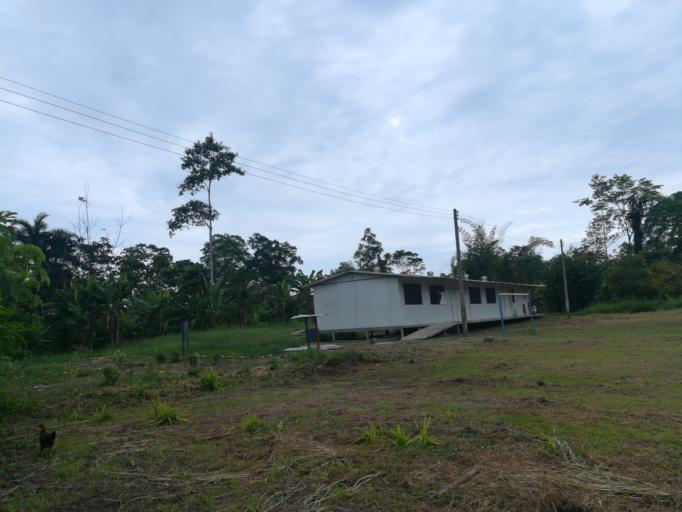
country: EC
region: Orellana
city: Boca Suno
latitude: -0.7499
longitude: -77.1538
